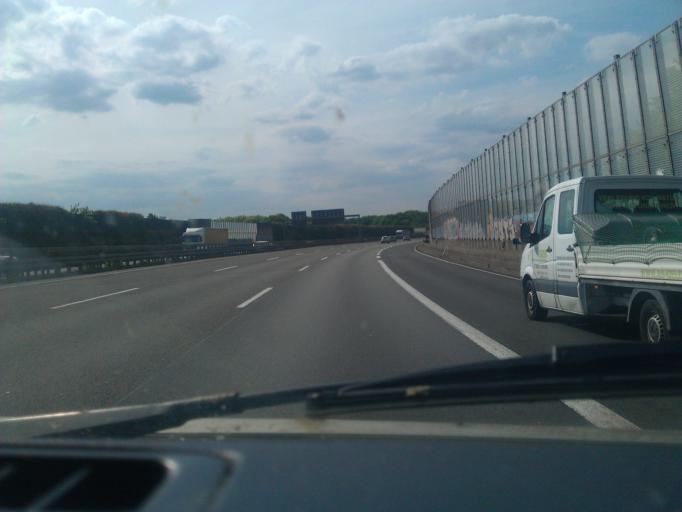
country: DE
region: North Rhine-Westphalia
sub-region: Regierungsbezirk Dusseldorf
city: Moers
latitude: 51.4817
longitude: 6.6711
